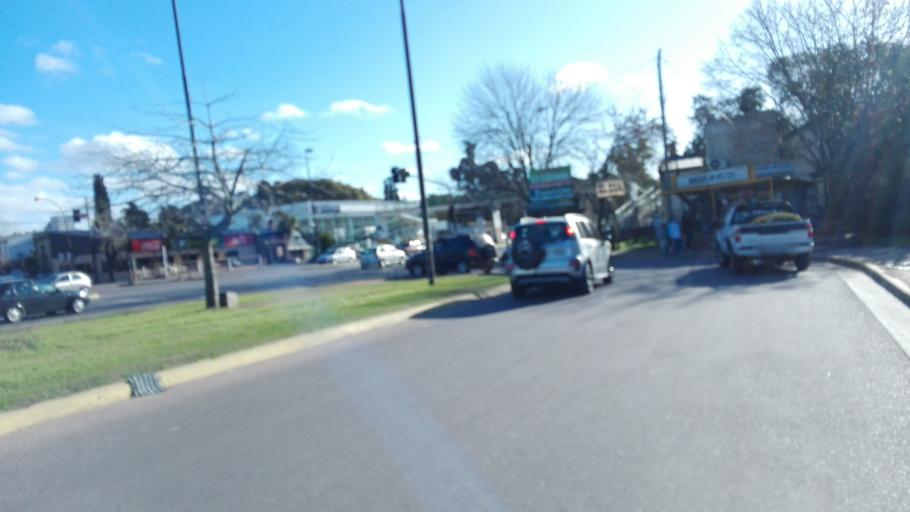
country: AR
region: Buenos Aires
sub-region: Partido de La Plata
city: La Plata
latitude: -34.8803
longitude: -58.0100
